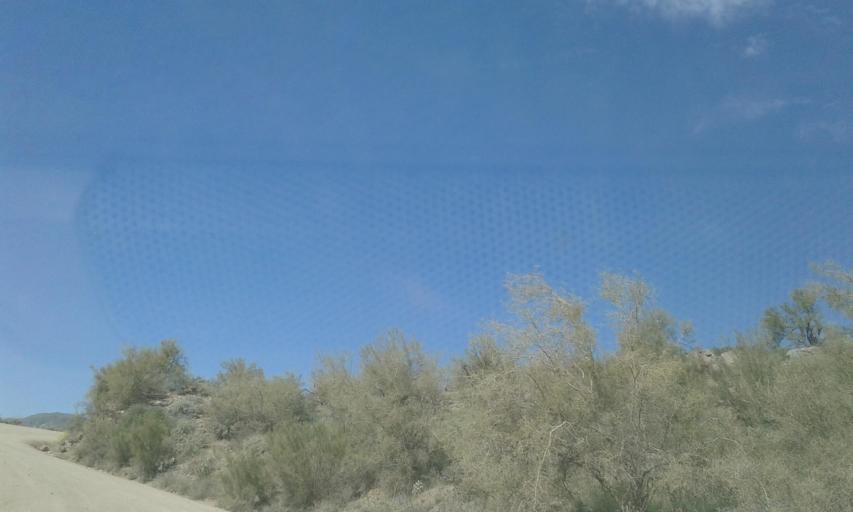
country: US
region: Arizona
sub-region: Gila County
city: Tonto Basin
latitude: 33.6010
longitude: -111.2036
